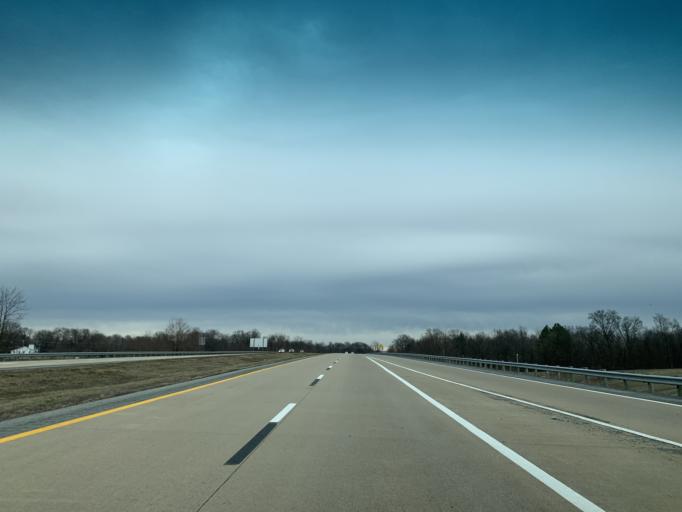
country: US
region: West Virginia
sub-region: Jefferson County
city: Ranson
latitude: 39.3789
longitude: -77.8918
